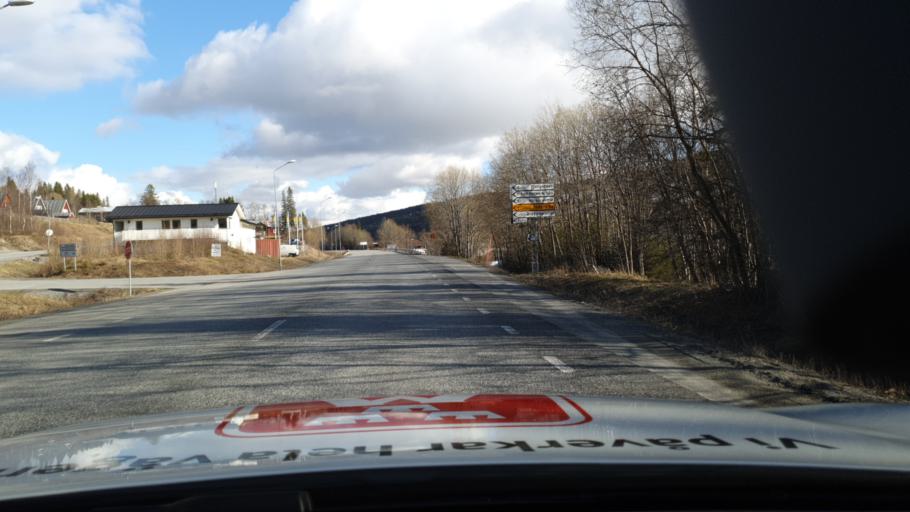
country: SE
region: Jaemtland
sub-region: Are Kommun
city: Are
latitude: 63.3937
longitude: 13.0933
